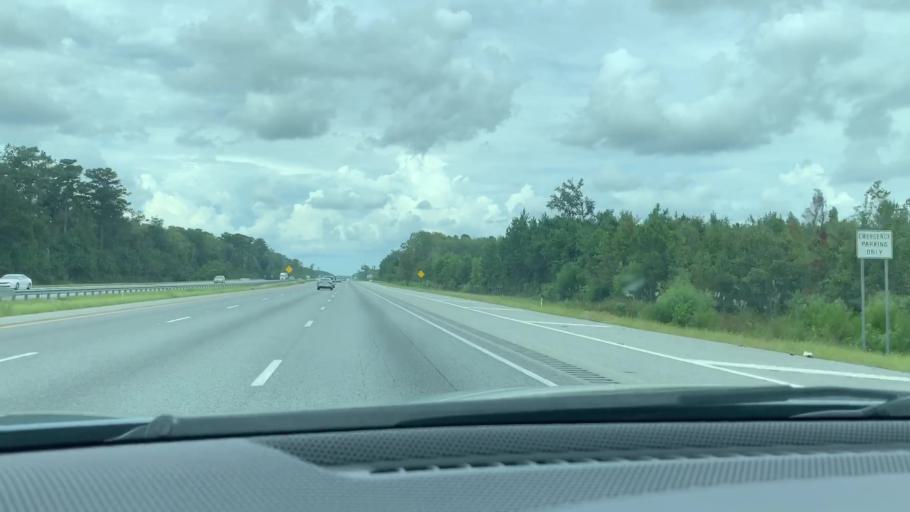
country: US
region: Georgia
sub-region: McIntosh County
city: Darien
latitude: 31.4384
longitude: -81.4441
